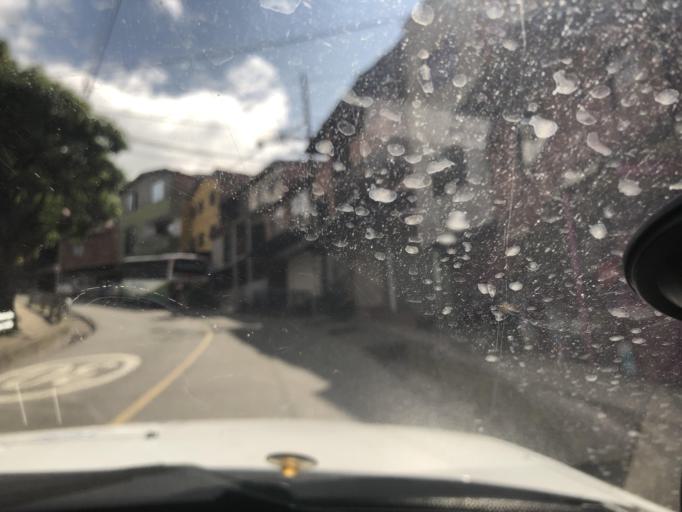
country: CO
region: Antioquia
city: Bello
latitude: 6.3092
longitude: -75.5484
